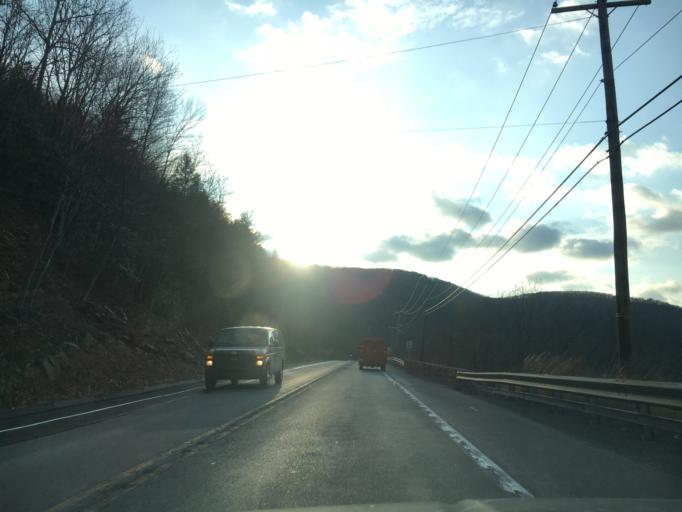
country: US
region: Pennsylvania
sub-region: Carbon County
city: Jim Thorpe
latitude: 40.8615
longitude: -75.7260
